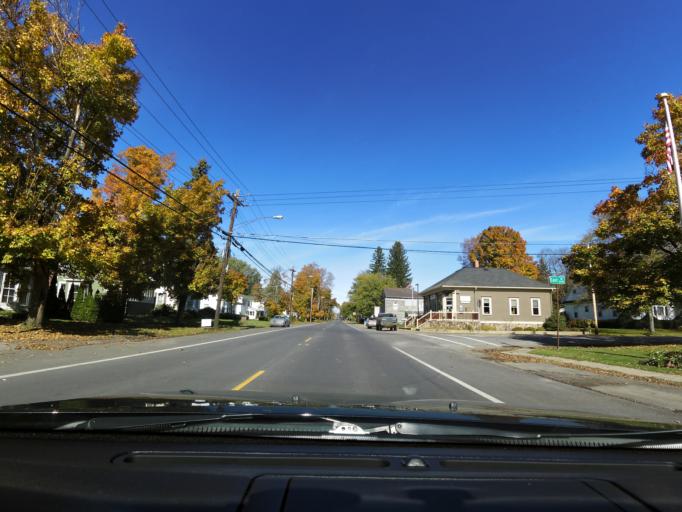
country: US
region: New York
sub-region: Wyoming County
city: Castile
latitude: 42.6408
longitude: -78.1341
